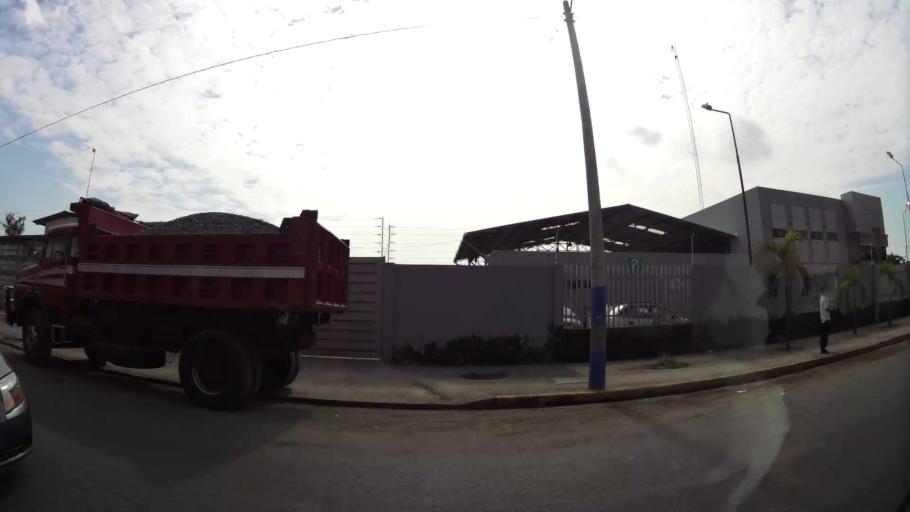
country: EC
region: Guayas
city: Guayaquil
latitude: -2.2510
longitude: -79.8782
